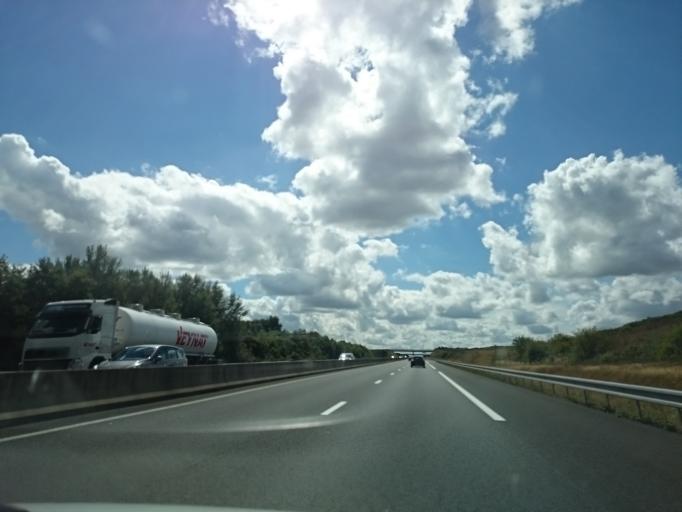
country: FR
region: Pays de la Loire
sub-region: Departement de Maine-et-Loire
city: Saint-Lambert-la-Potherie
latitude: 47.4723
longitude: -0.6801
